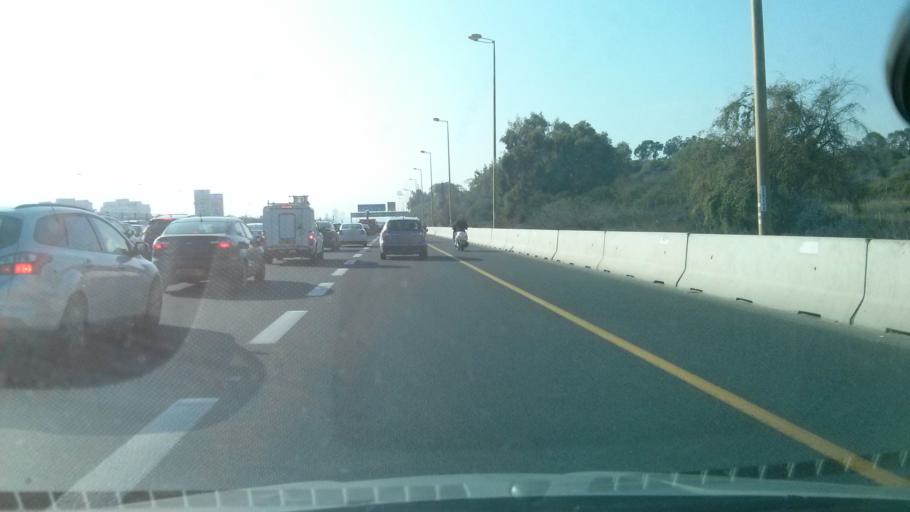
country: IL
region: Tel Aviv
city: Ramat HaSharon
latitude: 32.1297
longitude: 34.8098
